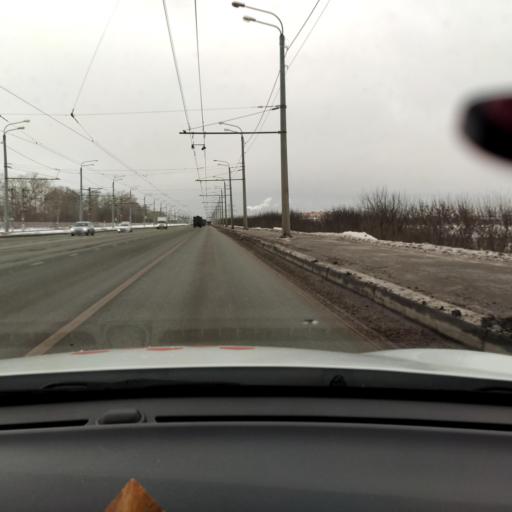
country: RU
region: Tatarstan
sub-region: Gorod Kazan'
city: Kazan
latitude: 55.7974
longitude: 49.0888
